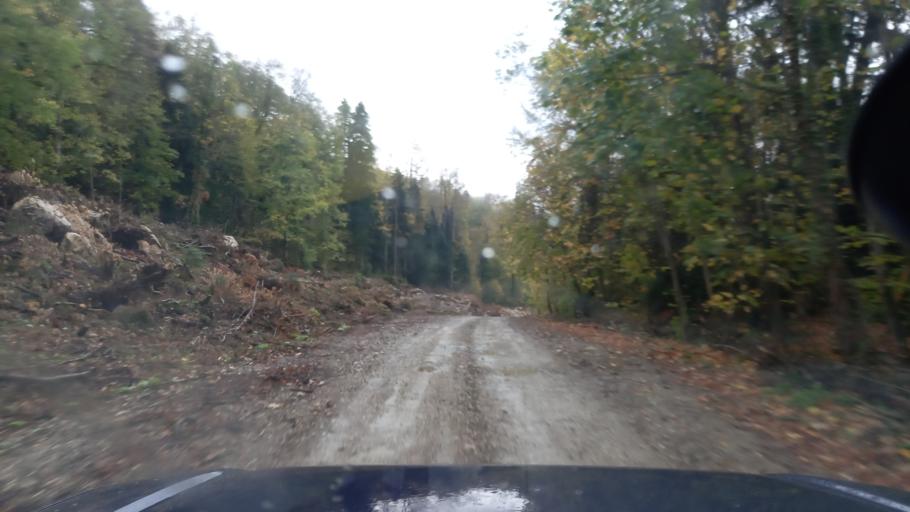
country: RU
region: Krasnodarskiy
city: Neftegorsk
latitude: 44.0460
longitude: 39.8336
